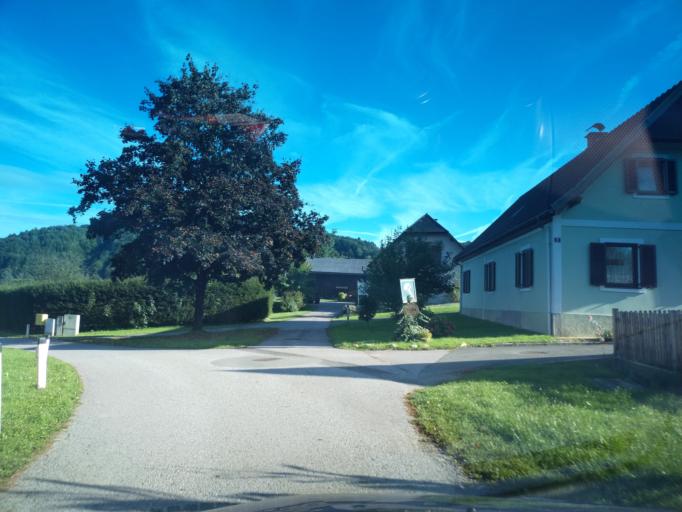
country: AT
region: Styria
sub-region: Politischer Bezirk Deutschlandsberg
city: Sankt Martin im Sulmtal
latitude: 46.7321
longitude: 15.3101
